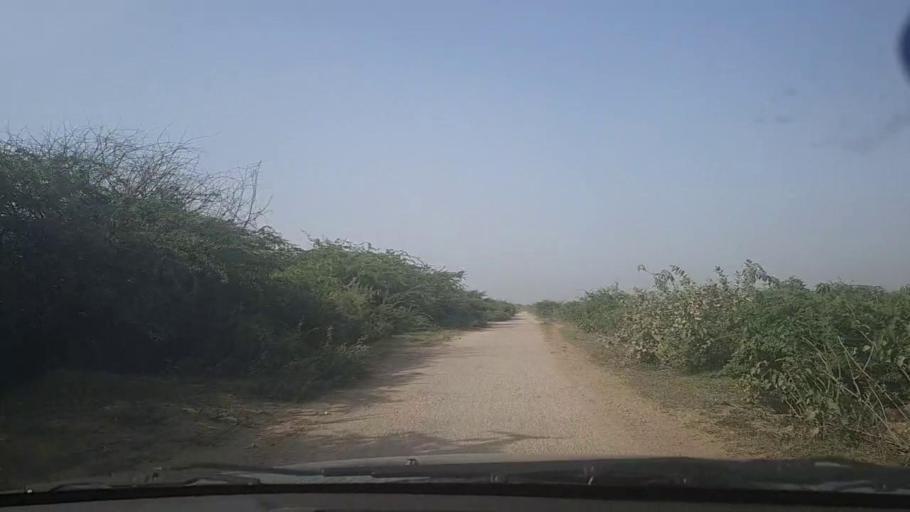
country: PK
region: Sindh
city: Keti Bandar
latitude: 24.2605
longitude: 67.5646
